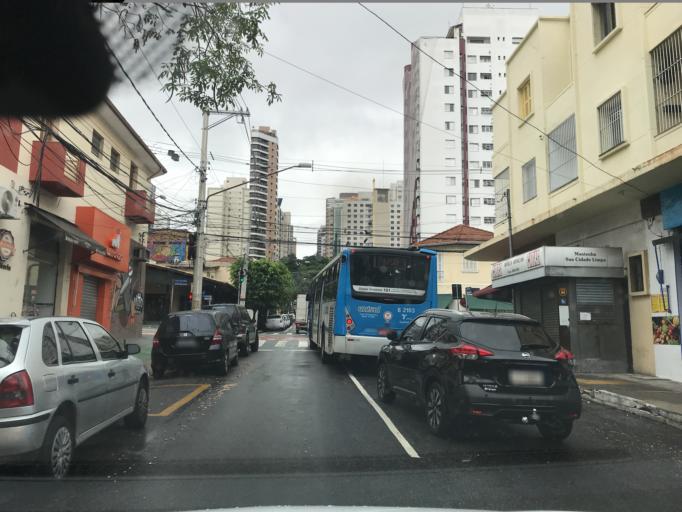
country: BR
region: Sao Paulo
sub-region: Sao Paulo
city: Sao Paulo
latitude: -23.5334
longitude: -46.6760
